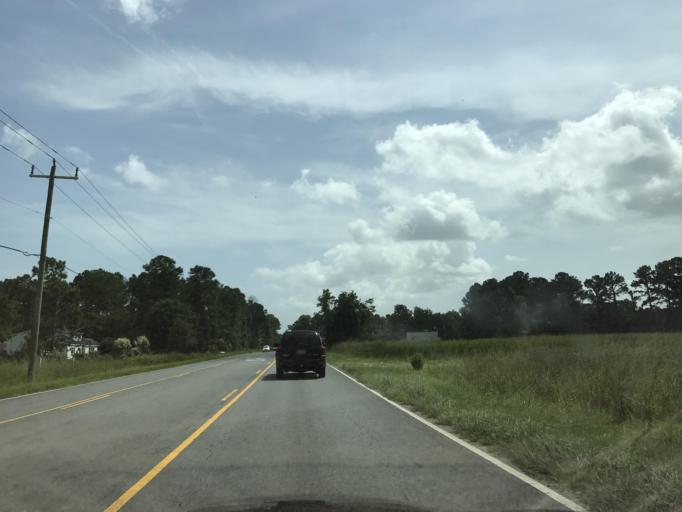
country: US
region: North Carolina
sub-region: New Hanover County
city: Wrightsboro
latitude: 34.3051
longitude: -77.9219
